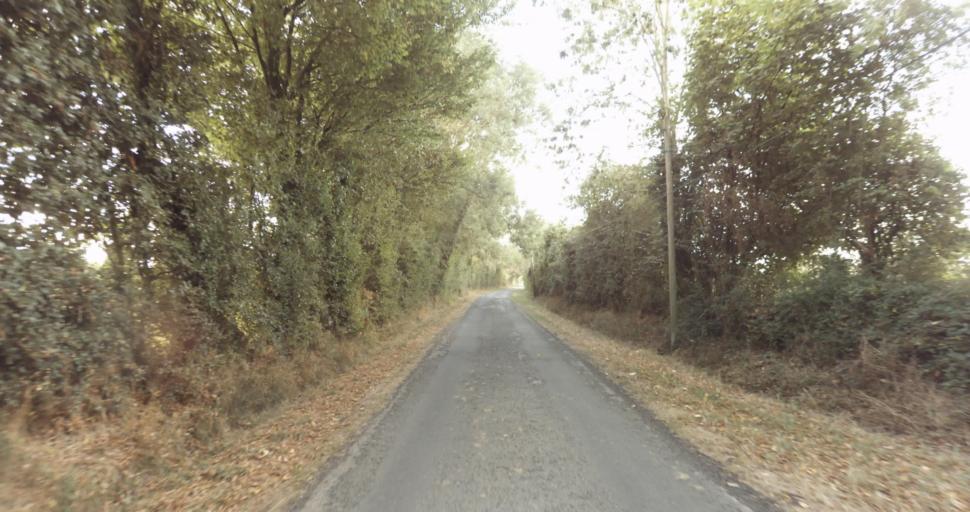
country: FR
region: Lower Normandy
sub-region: Departement de l'Orne
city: Vimoutiers
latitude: 48.9473
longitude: 0.2408
